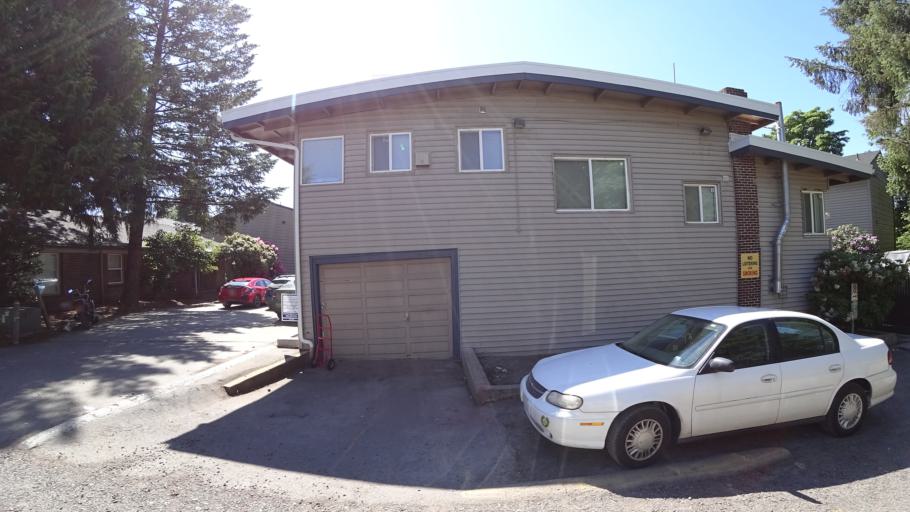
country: US
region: Oregon
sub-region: Washington County
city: Metzger
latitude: 45.4514
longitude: -122.7254
